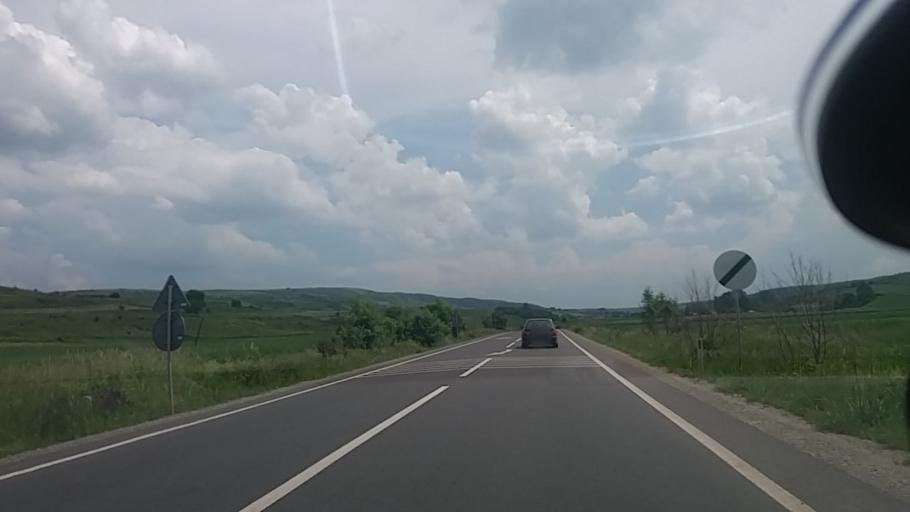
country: RO
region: Sibiu
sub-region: Comuna Seica Mare
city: Seica Mare
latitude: 45.9736
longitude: 24.1472
